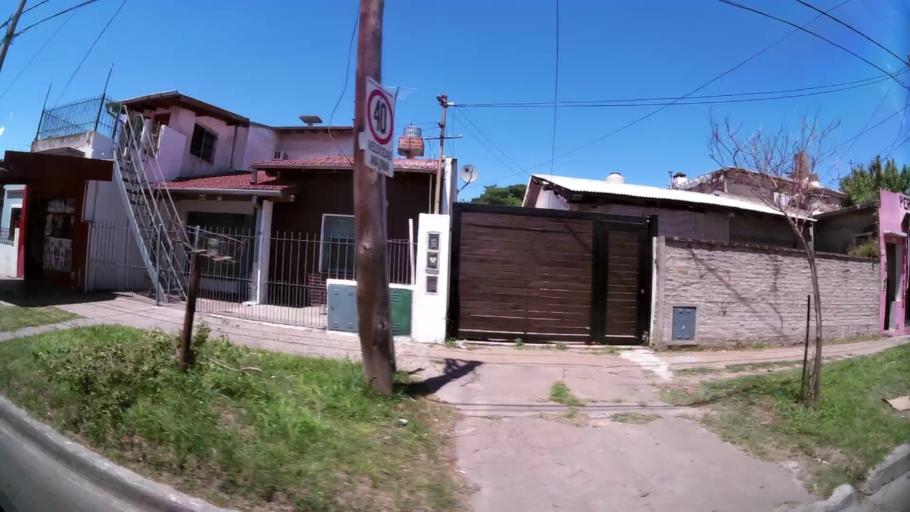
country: AR
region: Buenos Aires
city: Hurlingham
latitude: -34.5063
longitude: -58.6995
